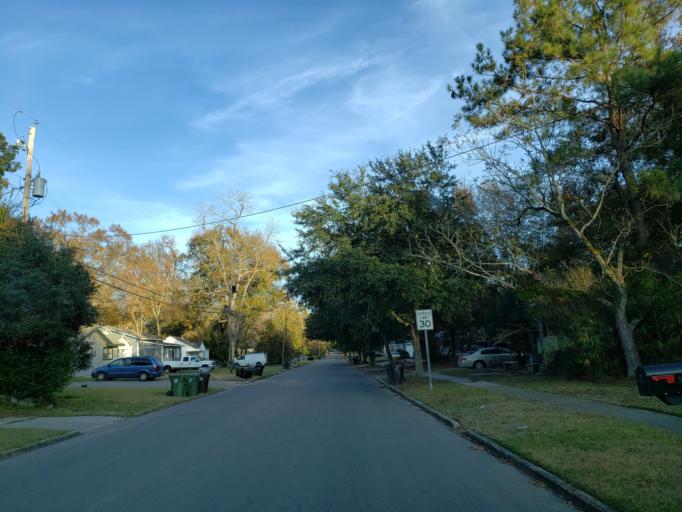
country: US
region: Mississippi
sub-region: Forrest County
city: Hattiesburg
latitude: 31.3302
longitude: -89.3038
